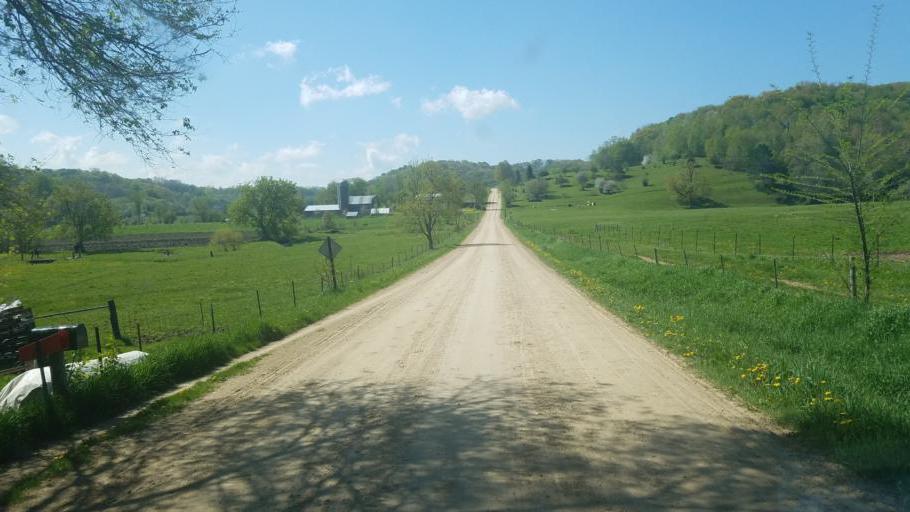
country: US
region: Wisconsin
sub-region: Vernon County
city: Hillsboro
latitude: 43.6145
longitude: -90.3919
